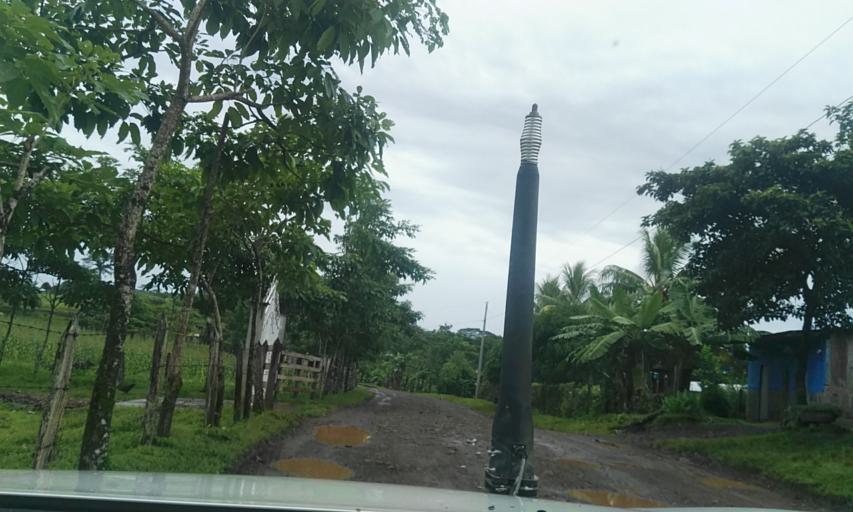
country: NI
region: Matagalpa
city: Rio Blanco
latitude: 12.9527
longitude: -85.1769
